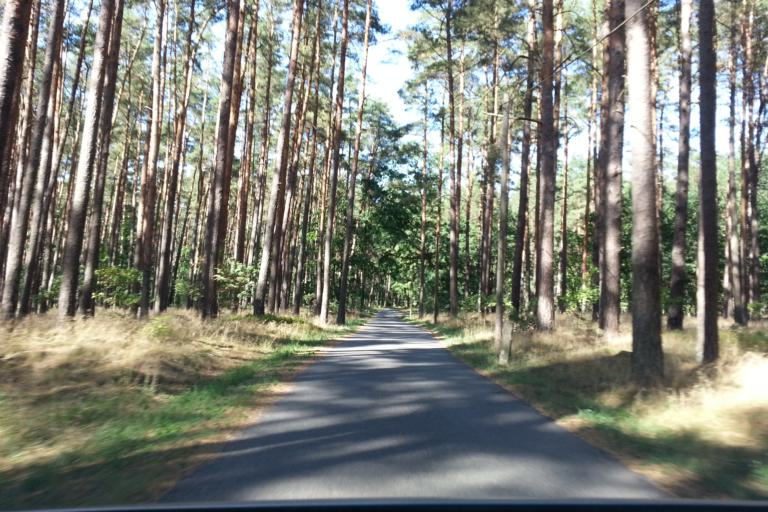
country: DE
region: Mecklenburg-Vorpommern
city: Eggesin
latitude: 53.6889
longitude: 14.0468
